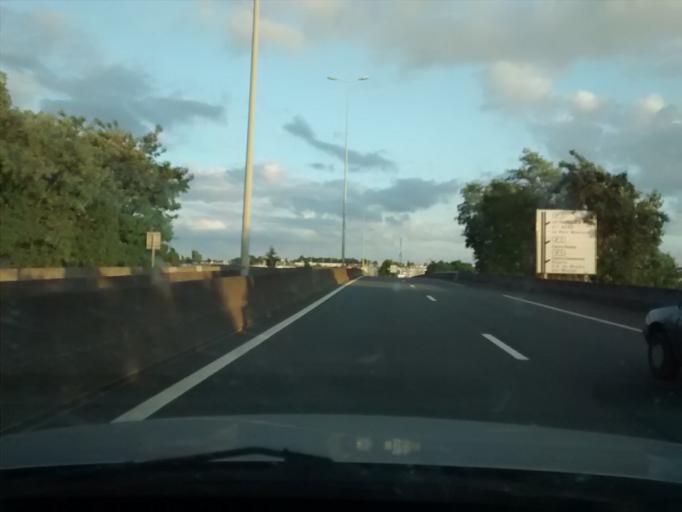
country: FR
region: Pays de la Loire
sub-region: Departement de la Sarthe
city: La Chapelle-Saint-Aubin
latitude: 48.0463
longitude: 0.1714
